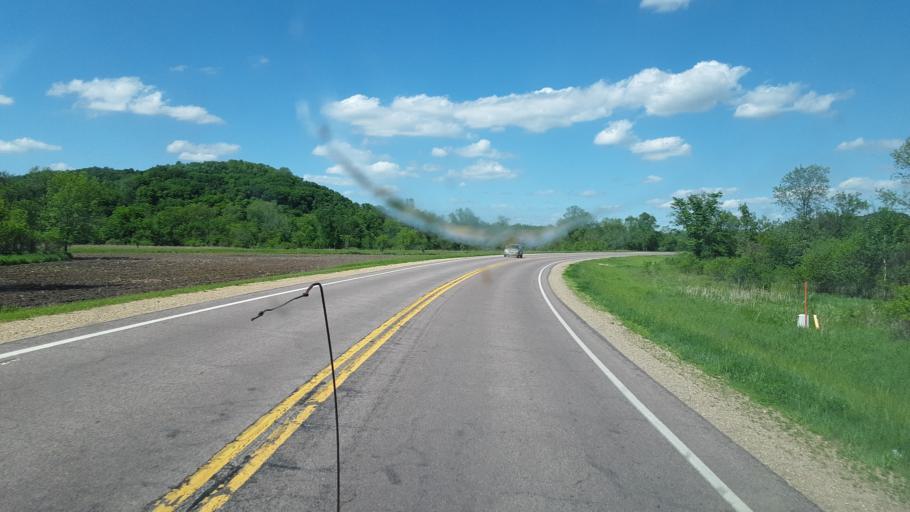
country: US
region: Wisconsin
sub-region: Richland County
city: Richland Center
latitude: 43.3730
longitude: -90.2663
